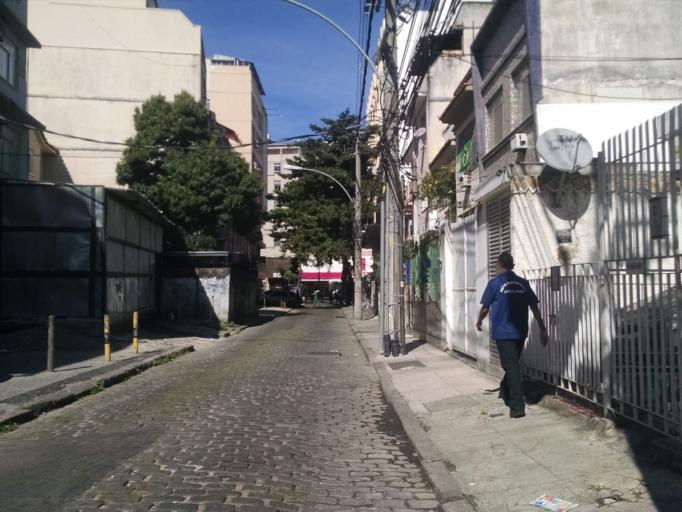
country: BR
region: Rio de Janeiro
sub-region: Rio De Janeiro
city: Rio de Janeiro
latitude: -22.9018
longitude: -43.2821
